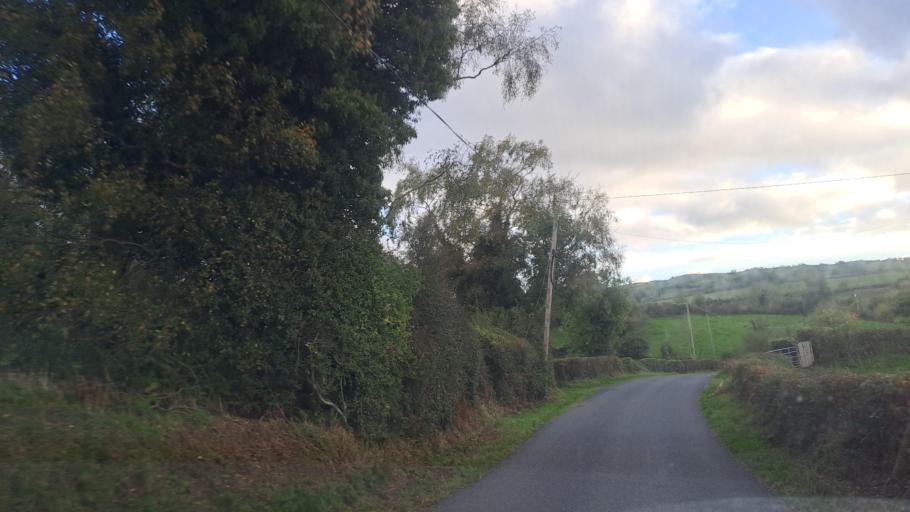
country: IE
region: Ulster
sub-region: County Monaghan
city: Castleblayney
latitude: 54.0366
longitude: -6.8107
